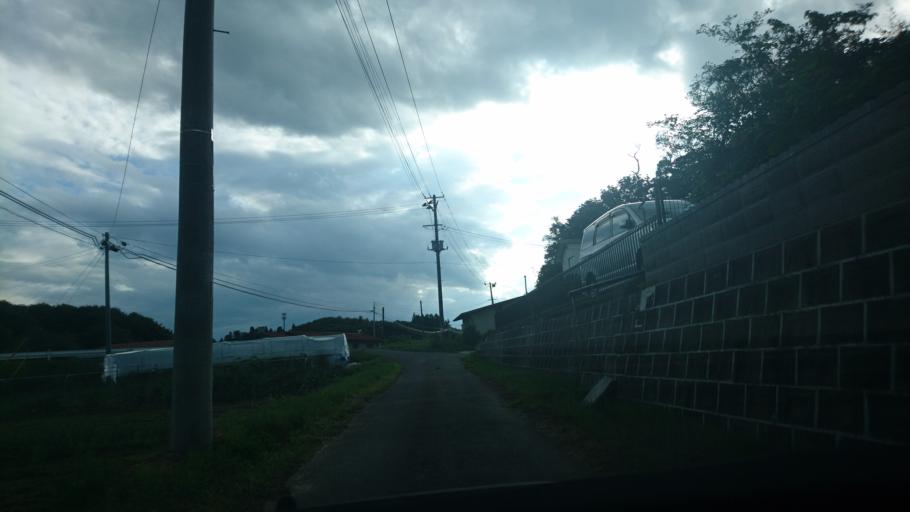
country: JP
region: Iwate
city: Ichinoseki
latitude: 38.8871
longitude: 141.1454
